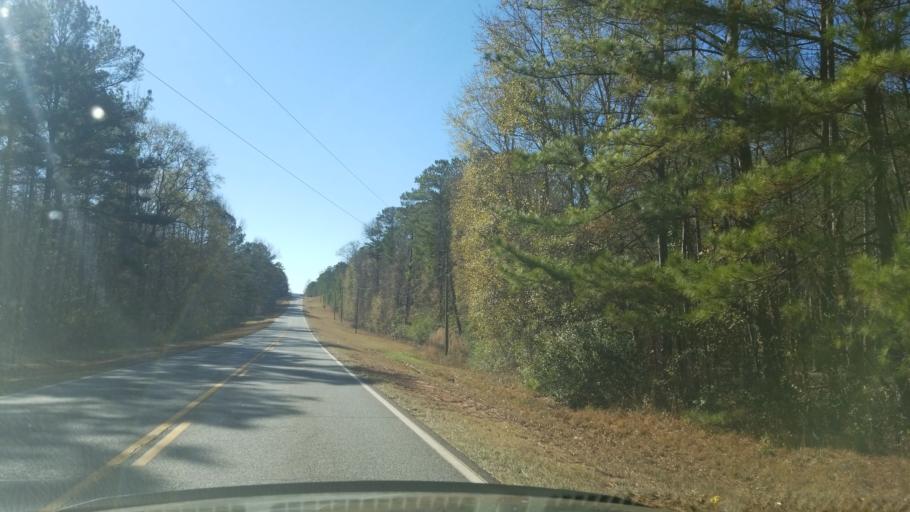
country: US
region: Georgia
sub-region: Talbot County
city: Sardis
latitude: 32.7884
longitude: -84.6797
